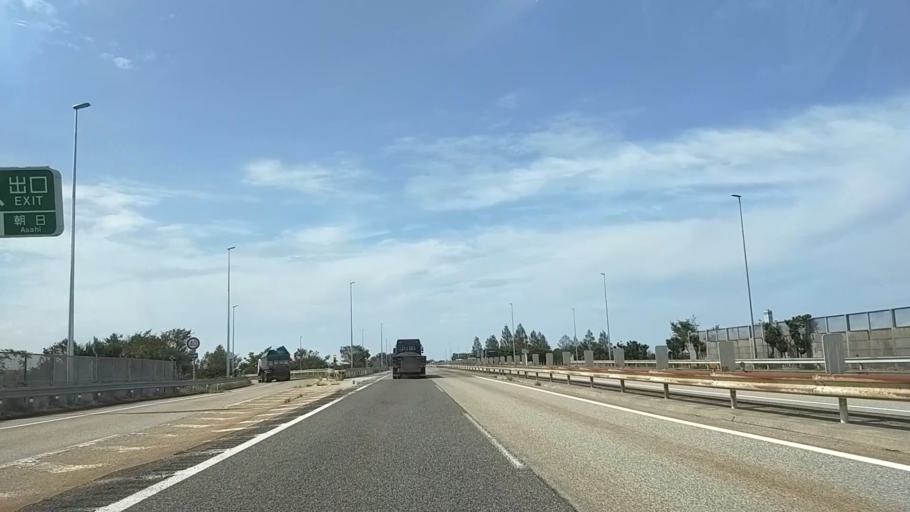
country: JP
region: Toyama
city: Nyuzen
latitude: 36.9414
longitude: 137.5529
